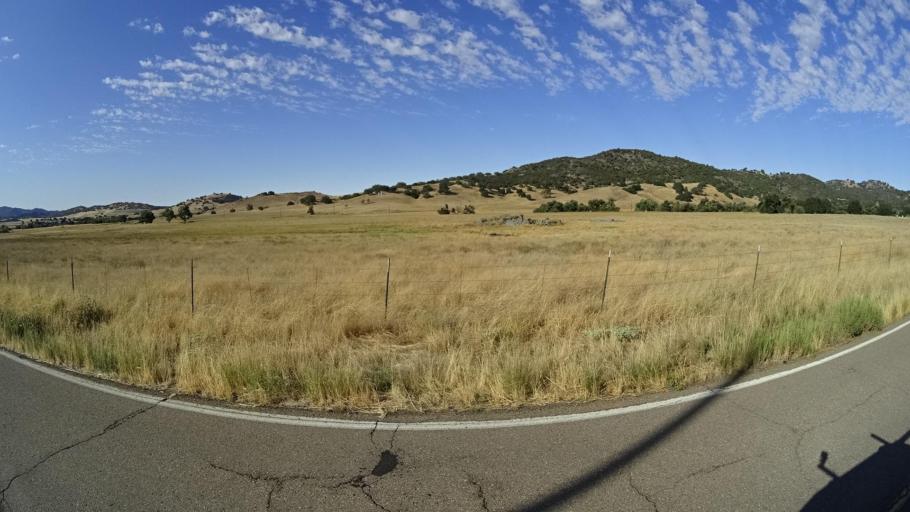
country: US
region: California
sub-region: San Diego County
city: Julian
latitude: 33.1402
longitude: -116.6829
